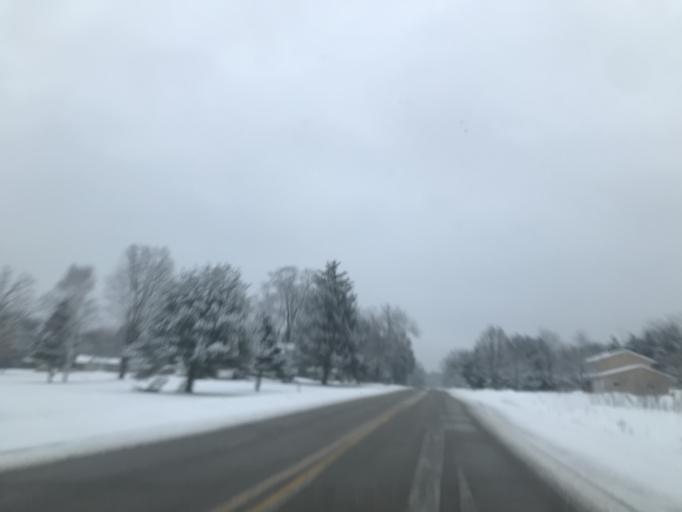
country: US
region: Wisconsin
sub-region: Oconto County
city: Oconto Falls
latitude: 44.8636
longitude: -88.1215
